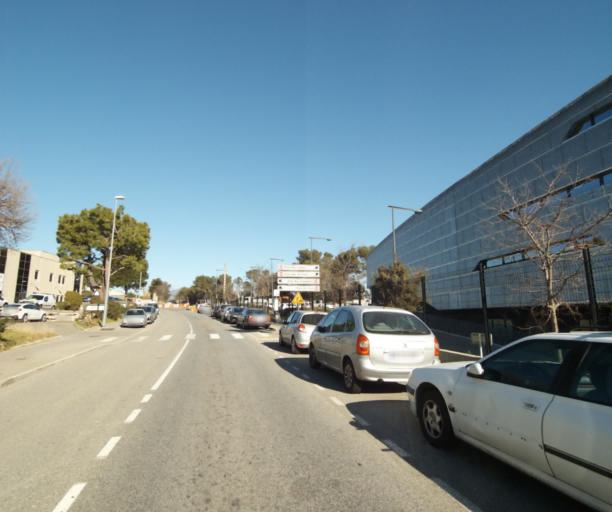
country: FR
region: Provence-Alpes-Cote d'Azur
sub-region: Departement des Alpes-Maritimes
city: Biot
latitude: 43.6060
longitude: 7.0760
